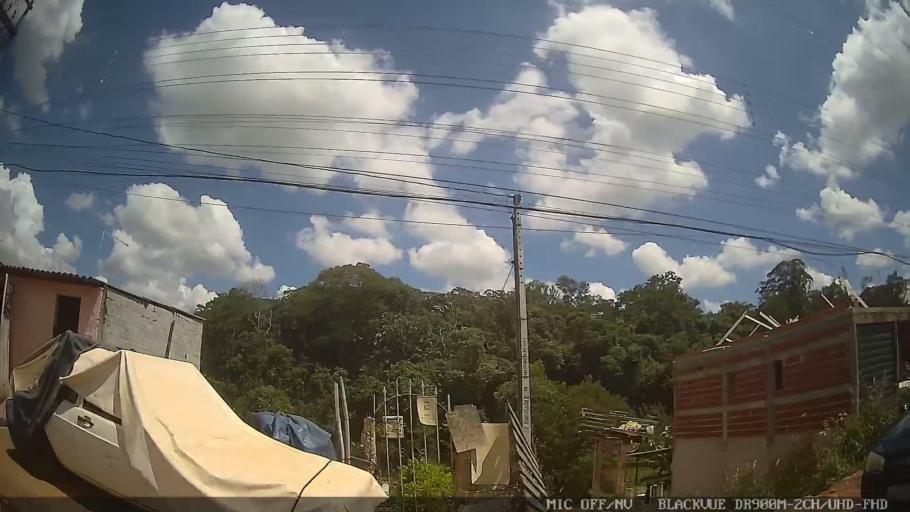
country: BR
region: Sao Paulo
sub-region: Atibaia
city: Atibaia
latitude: -23.1599
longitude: -46.6255
